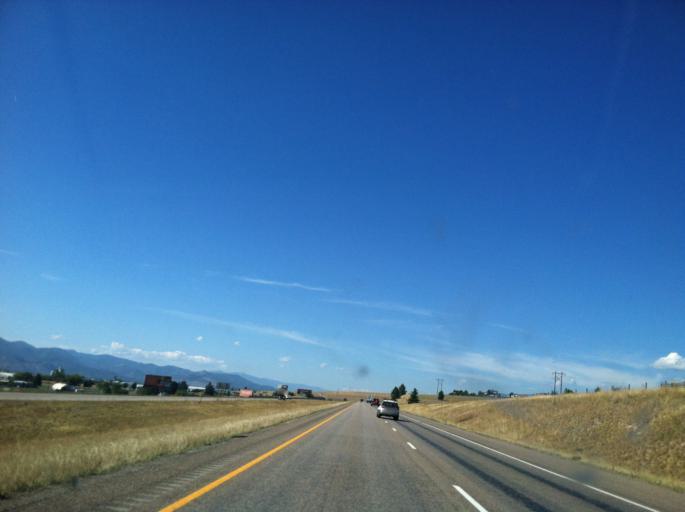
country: US
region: Montana
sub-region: Missoula County
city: Orchard Homes
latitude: 46.9310
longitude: -114.0835
